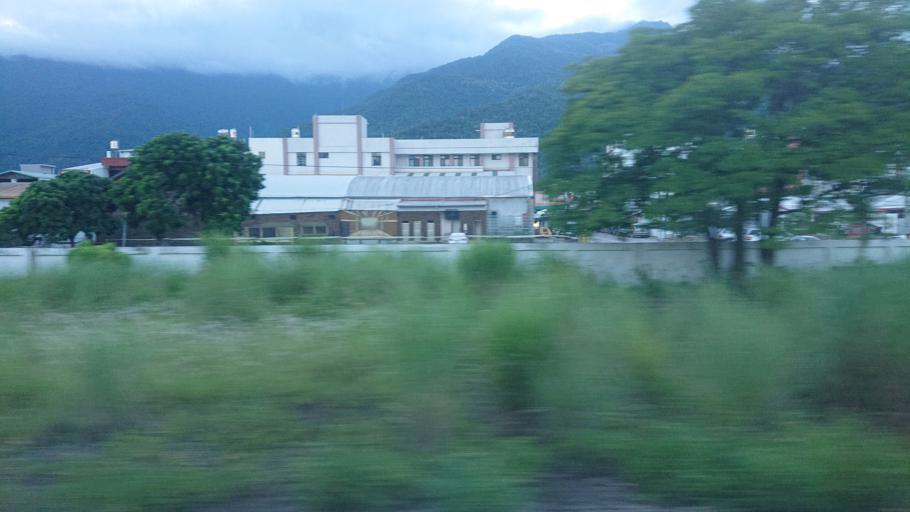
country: TW
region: Taiwan
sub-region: Taitung
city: Taitung
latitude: 23.0476
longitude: 121.1651
